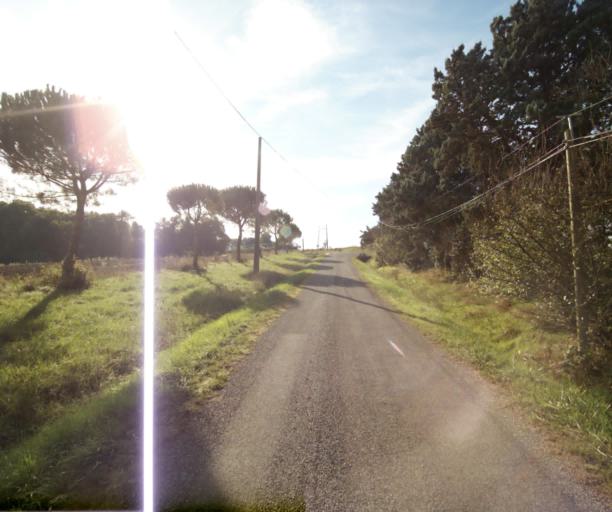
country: FR
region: Midi-Pyrenees
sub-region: Departement du Tarn-et-Garonne
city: Nohic
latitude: 43.9062
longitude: 1.4650
